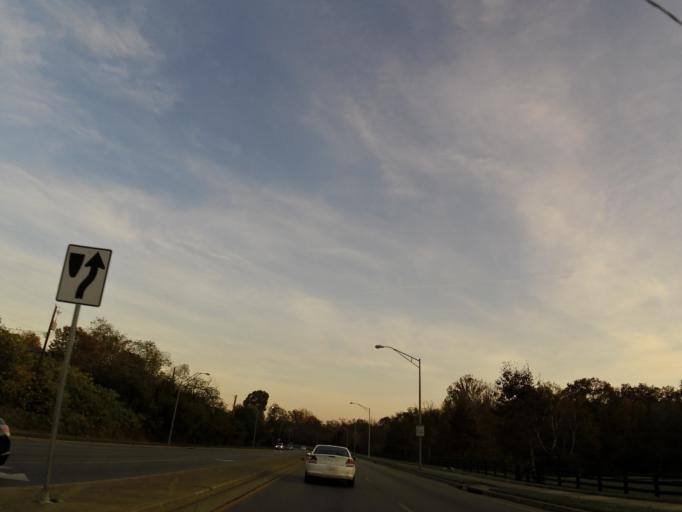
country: US
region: Kentucky
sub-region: Fayette County
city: Lexington
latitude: 37.9703
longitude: -84.5107
